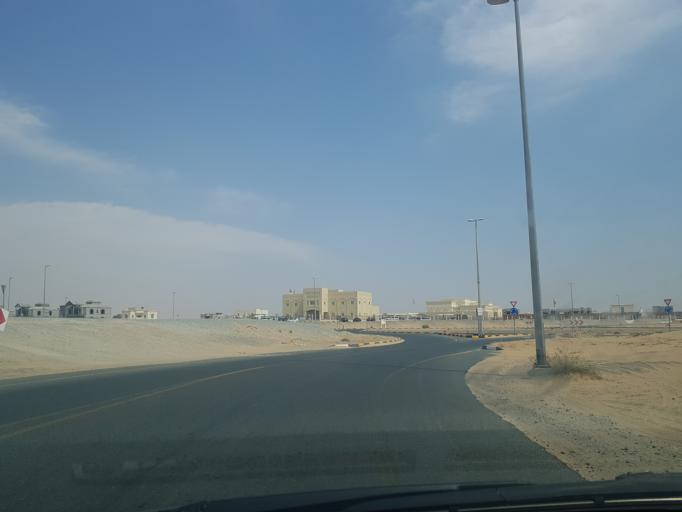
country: AE
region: Ash Shariqah
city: Sharjah
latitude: 25.2275
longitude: 55.5991
